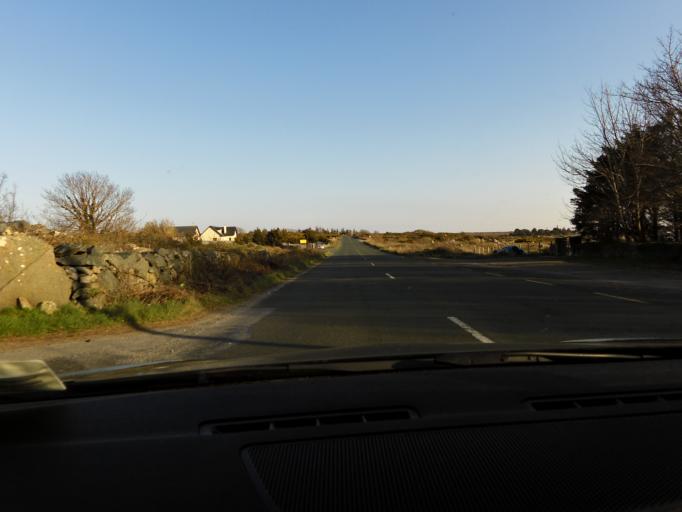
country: IE
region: Connaught
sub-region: County Galway
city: Oughterard
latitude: 53.2843
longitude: -9.5423
